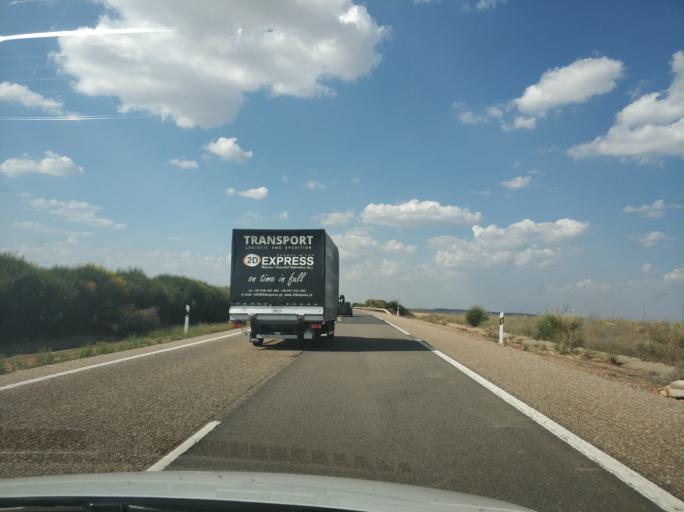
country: ES
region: Castille and Leon
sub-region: Provincia de Zamora
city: Matilla de Arzon
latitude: 42.0817
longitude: -5.6551
